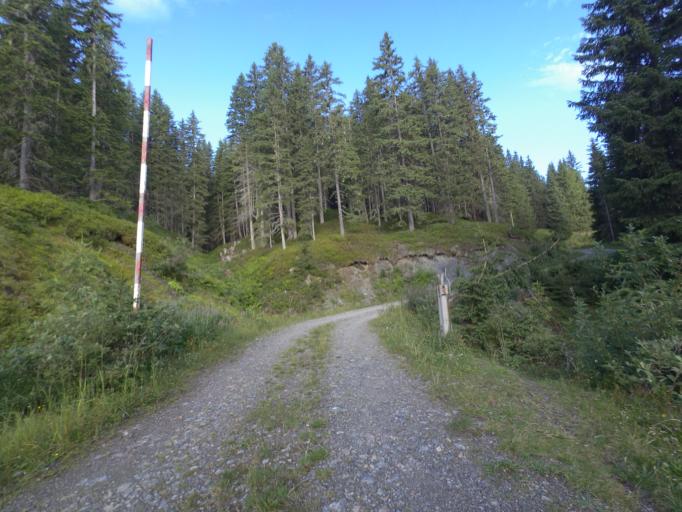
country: AT
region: Salzburg
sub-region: Politischer Bezirk Sankt Johann im Pongau
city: Goldegg
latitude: 47.3498
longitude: 13.0917
